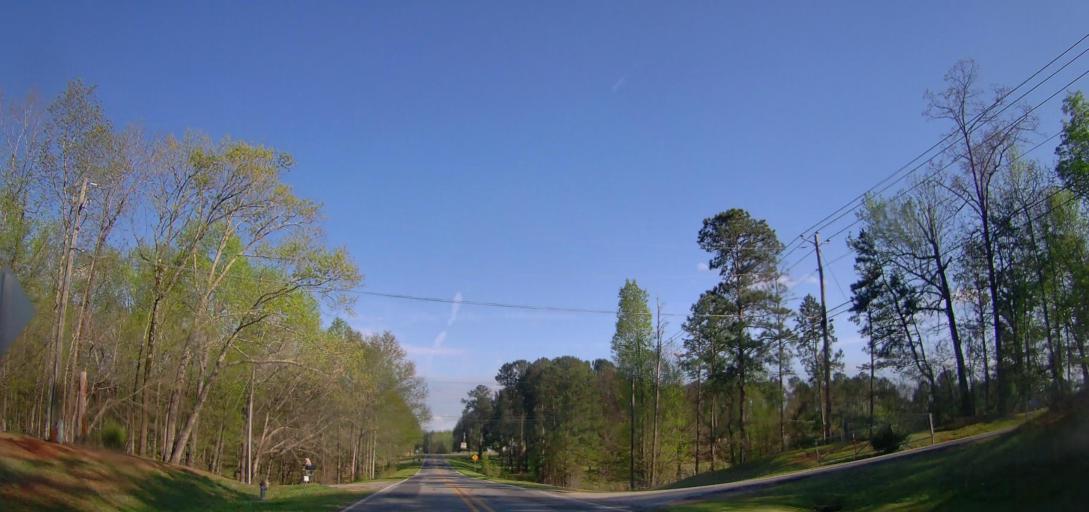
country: US
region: Georgia
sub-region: Baldwin County
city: Milledgeville
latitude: 33.1487
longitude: -83.2577
